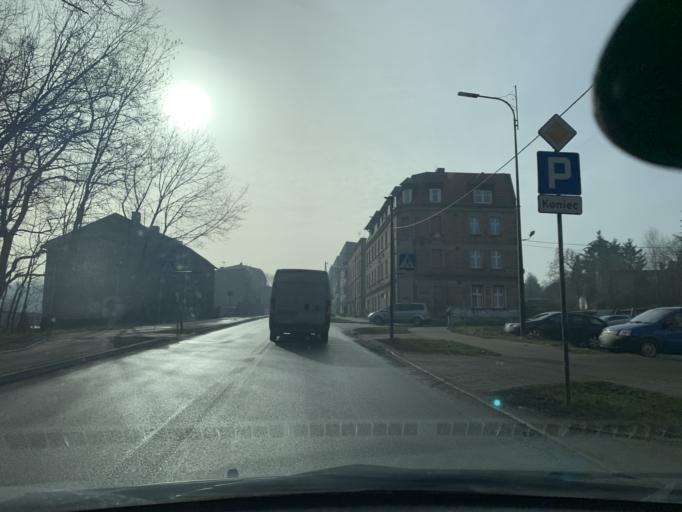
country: PL
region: Silesian Voivodeship
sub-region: Ruda Slaska
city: Ruda Slaska
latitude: 50.3241
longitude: 18.8559
